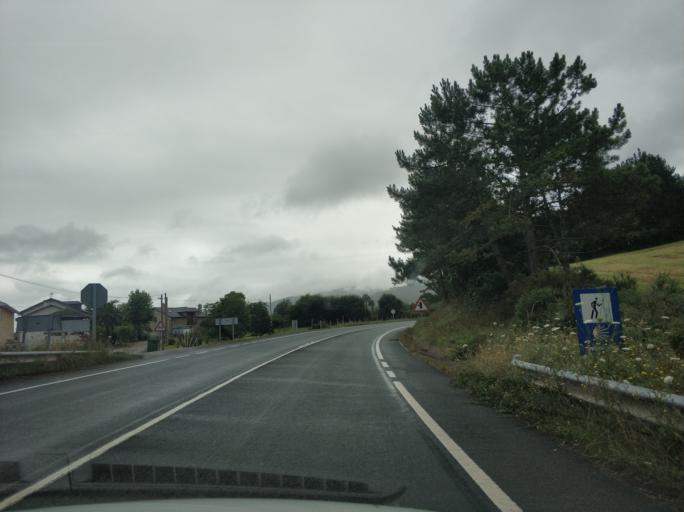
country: ES
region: Asturias
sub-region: Province of Asturias
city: Tineo
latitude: 43.5460
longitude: -6.4352
